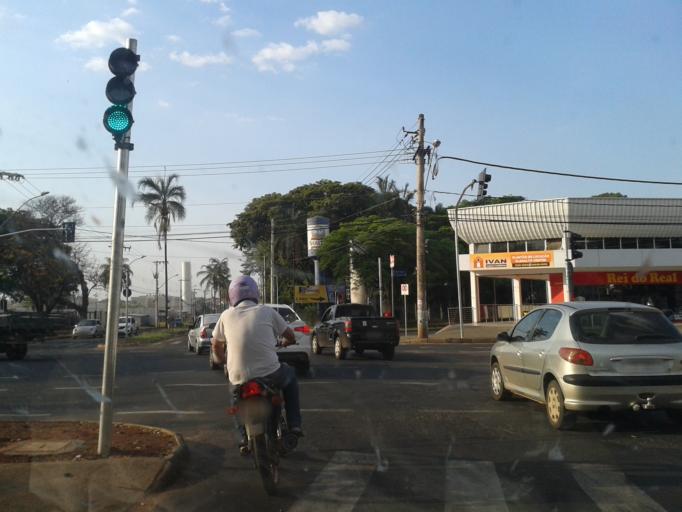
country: BR
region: Minas Gerais
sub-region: Uberlandia
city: Uberlandia
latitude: -18.9296
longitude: -48.3203
